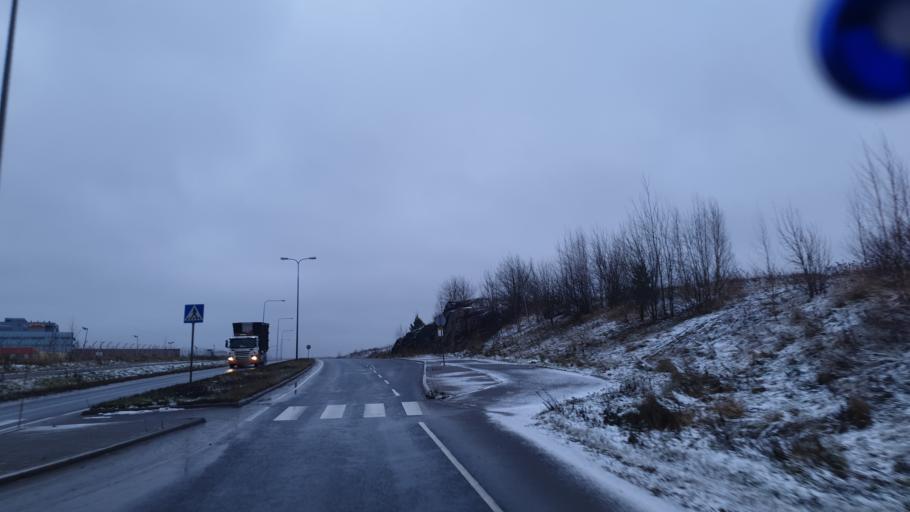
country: FI
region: Uusimaa
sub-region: Helsinki
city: Vantaa
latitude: 60.3167
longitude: 24.9042
